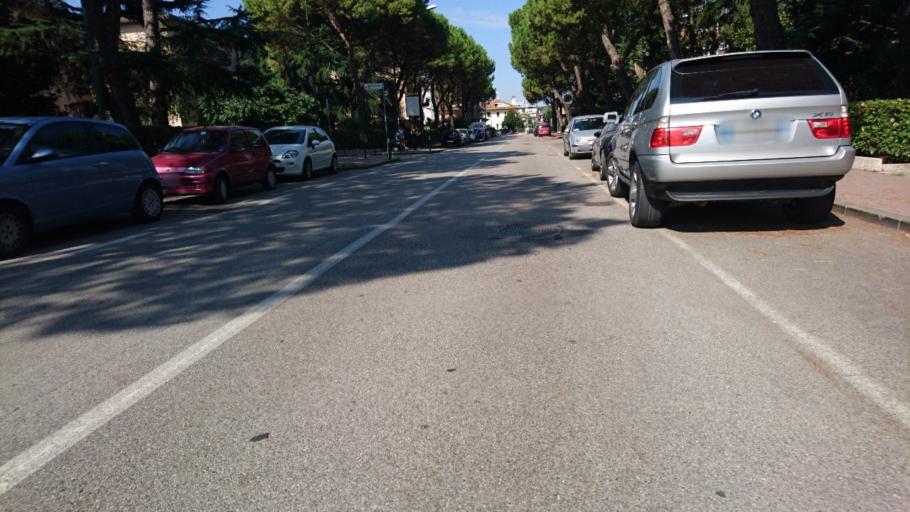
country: IT
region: Veneto
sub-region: Provincia di Venezia
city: Mestre
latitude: 45.5085
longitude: 12.2565
